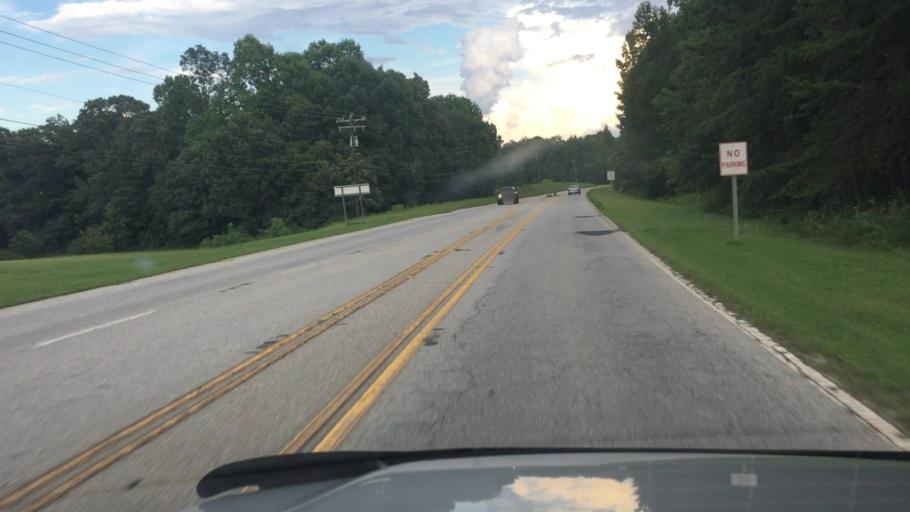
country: US
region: South Carolina
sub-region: Spartanburg County
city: Mayo
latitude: 35.1417
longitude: -81.8153
